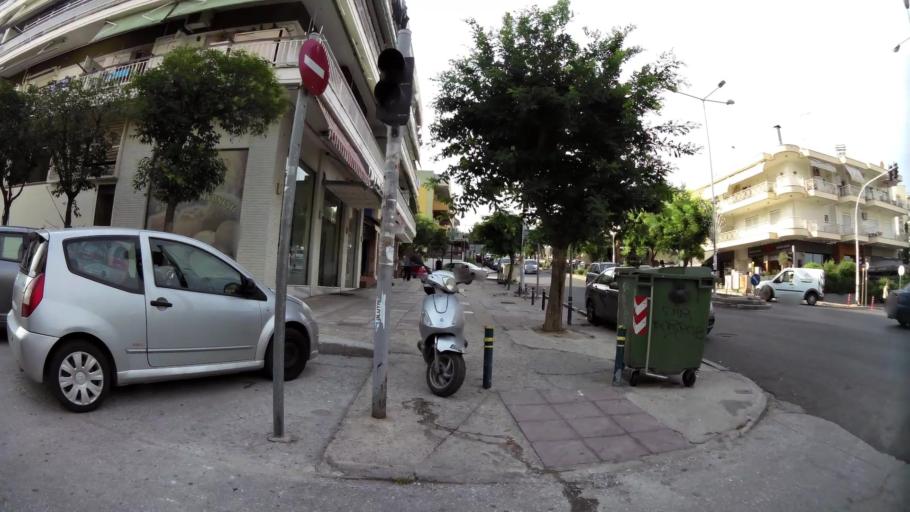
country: GR
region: Central Macedonia
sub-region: Nomos Thessalonikis
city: Sykies
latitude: 40.6508
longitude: 22.9582
